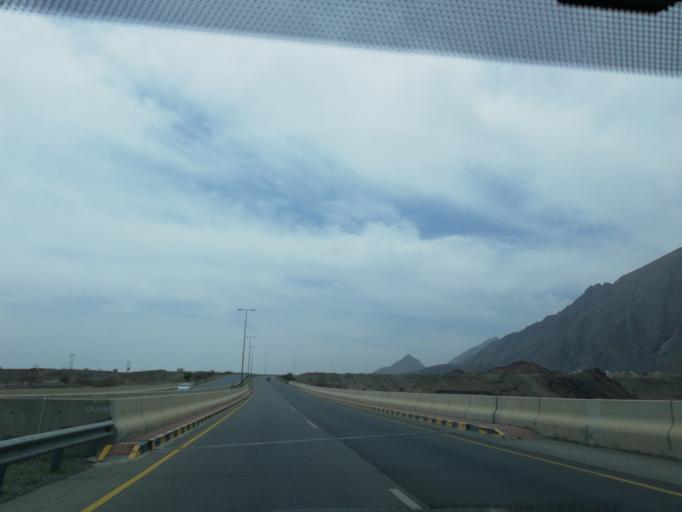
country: OM
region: Muhafazat ad Dakhiliyah
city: Izki
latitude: 23.1102
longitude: 57.8318
